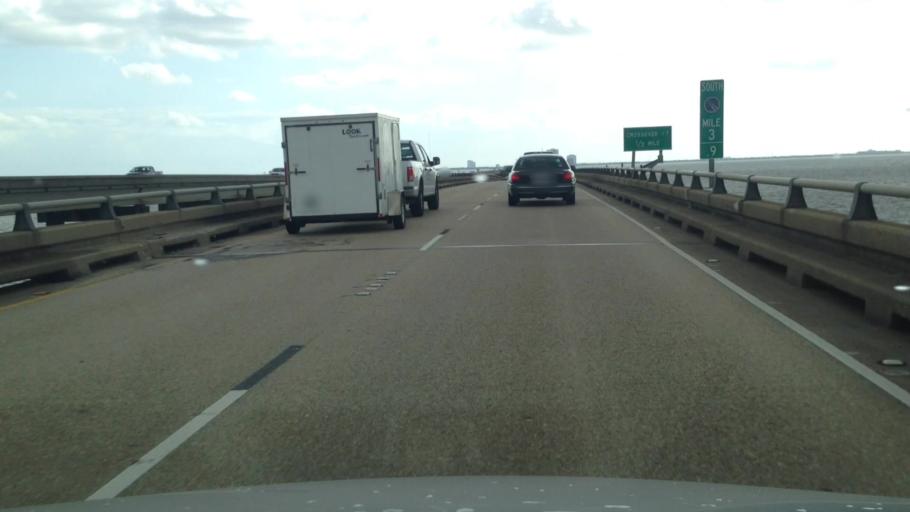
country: US
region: Louisiana
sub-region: Jefferson Parish
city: Metairie
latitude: 30.0779
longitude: -90.1443
